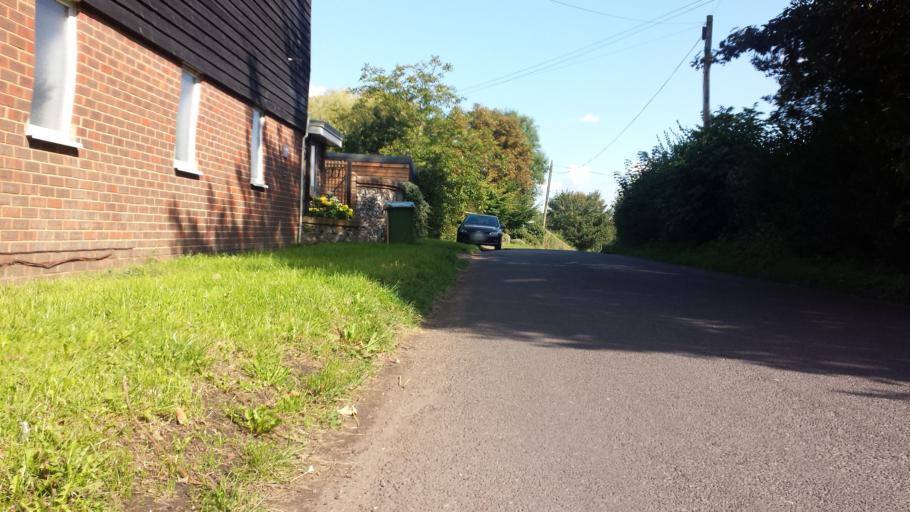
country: GB
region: England
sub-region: Kent
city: Shoreham
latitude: 51.3527
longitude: 0.1651
